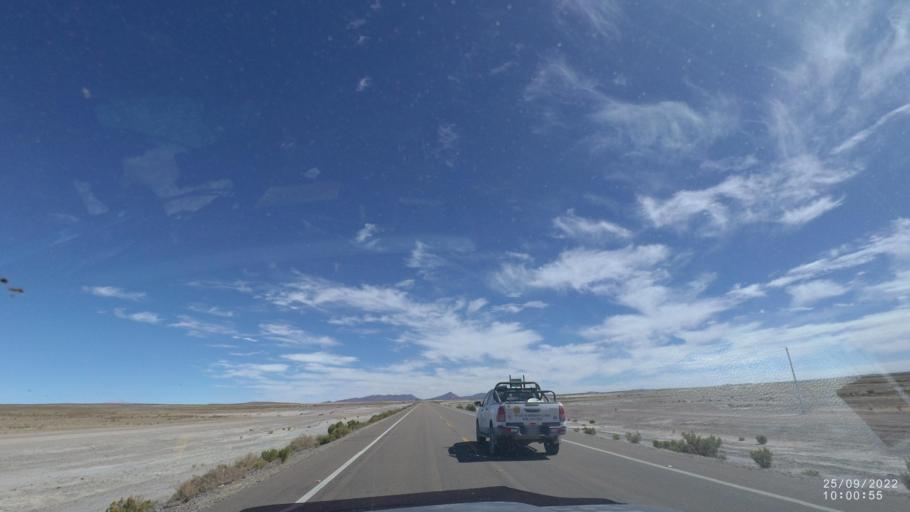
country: BO
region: Potosi
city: Colchani
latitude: -20.2654
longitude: -66.9517
